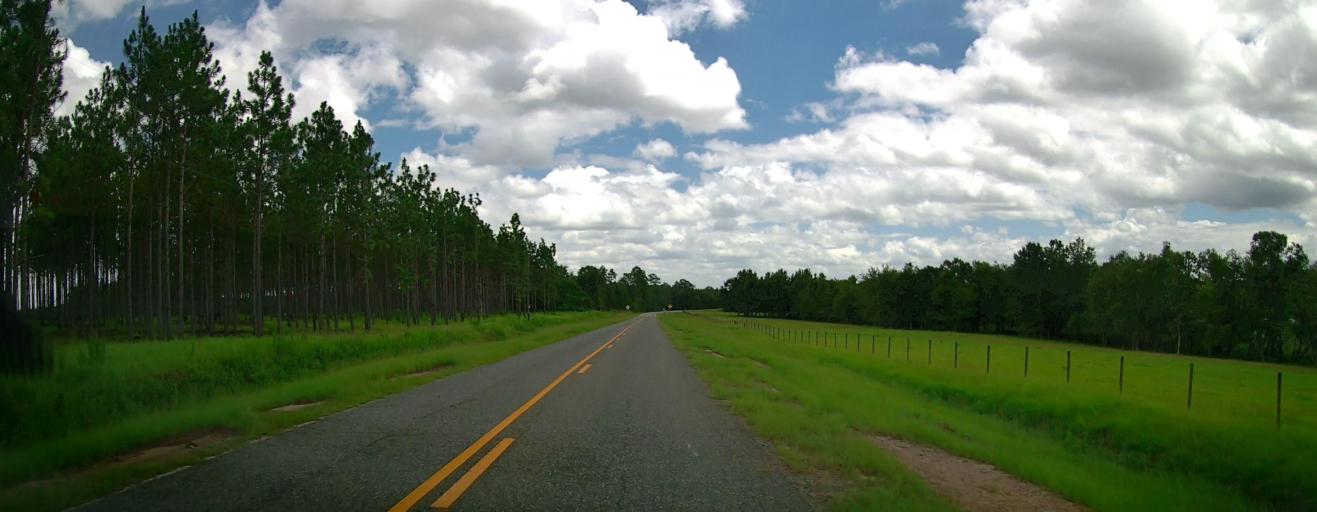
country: US
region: Georgia
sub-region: Turner County
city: Ashburn
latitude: 31.6970
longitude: -83.4827
